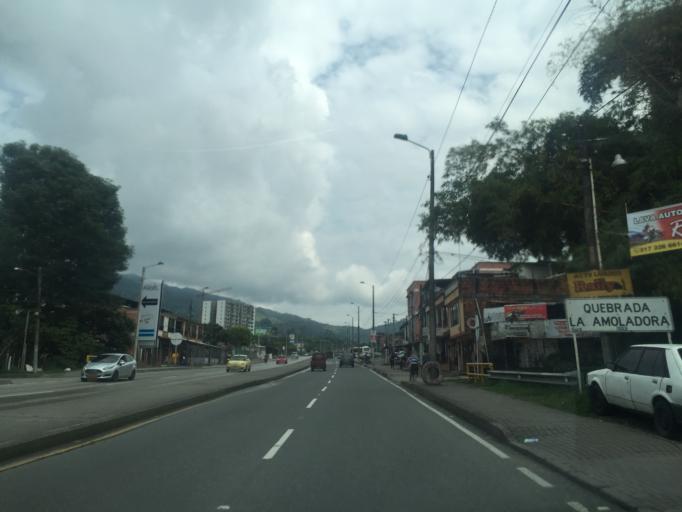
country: CO
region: Risaralda
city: Dos Quebradas
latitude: 4.8422
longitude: -75.6728
